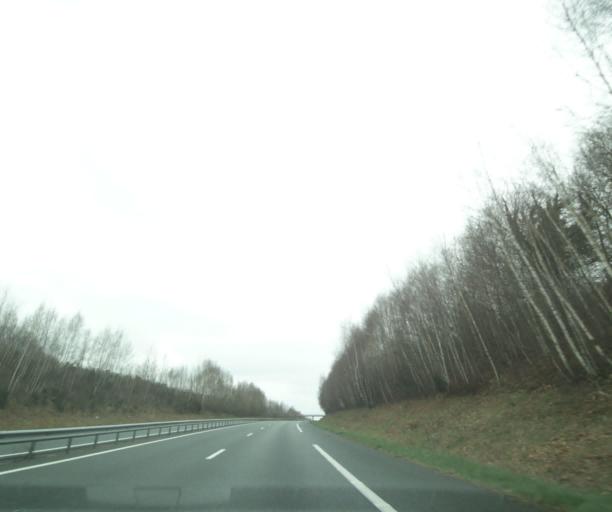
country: FR
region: Limousin
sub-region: Departement de la Haute-Vienne
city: Saint-Sulpice-les-Feuilles
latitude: 46.3725
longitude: 1.4436
